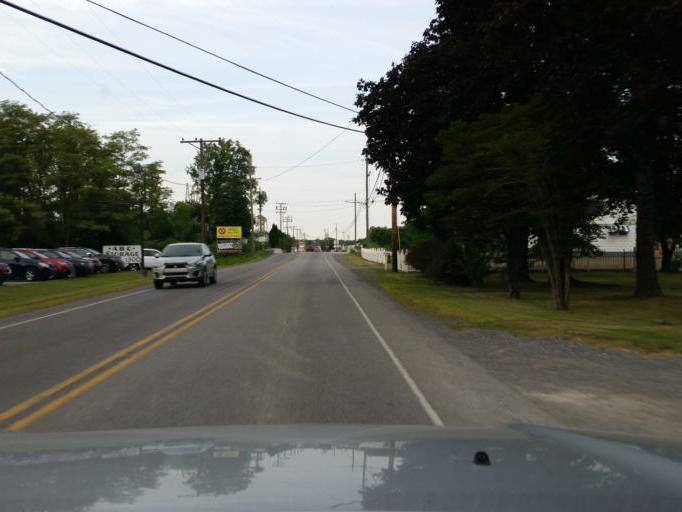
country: US
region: Pennsylvania
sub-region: Blair County
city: Lakemont
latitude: 40.4671
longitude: -78.4264
